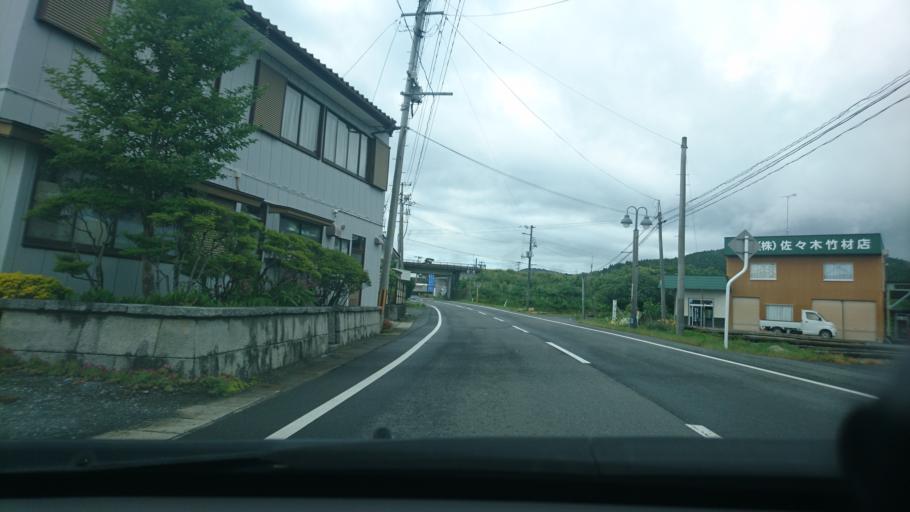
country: JP
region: Miyagi
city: Wakuya
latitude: 38.6079
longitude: 141.3010
